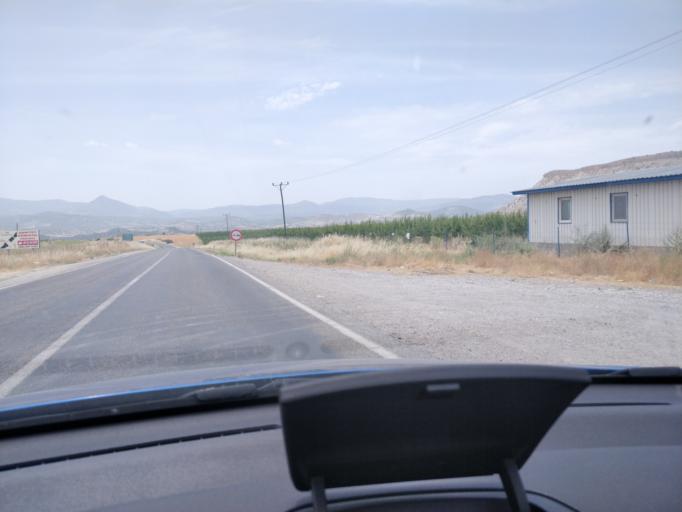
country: TR
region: Mersin
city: Mut
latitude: 36.5959
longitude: 33.4323
